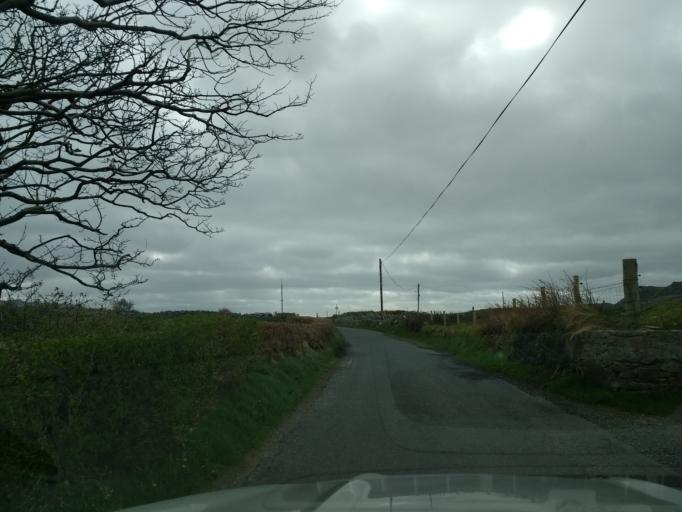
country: IE
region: Ulster
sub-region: County Donegal
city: Buncrana
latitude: 55.2482
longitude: -7.6226
